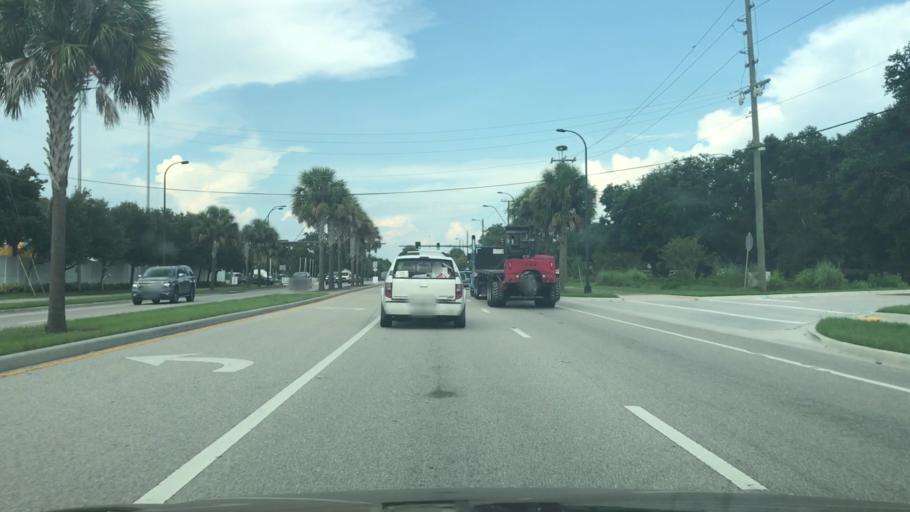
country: US
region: Florida
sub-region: Sarasota County
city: Fruitville
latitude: 27.3384
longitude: -82.4282
